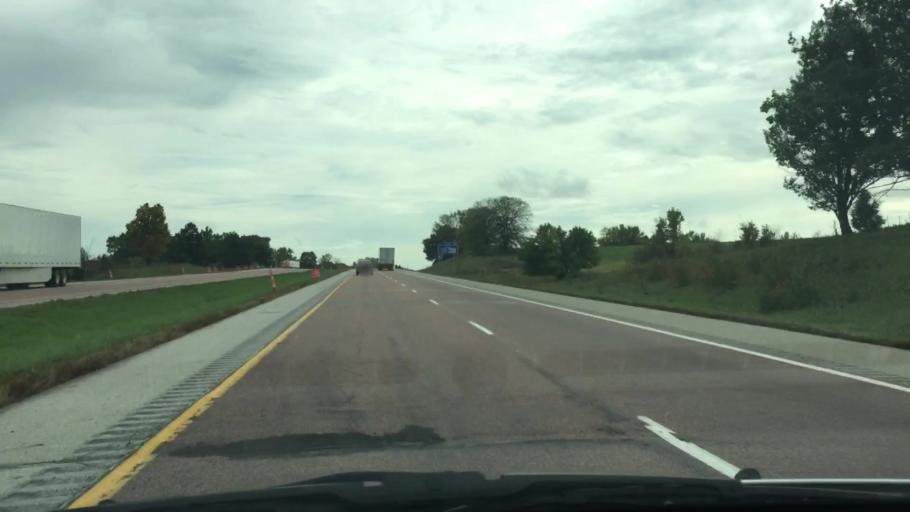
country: US
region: Iowa
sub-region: Warren County
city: Norwalk
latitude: 41.3163
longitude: -93.7791
